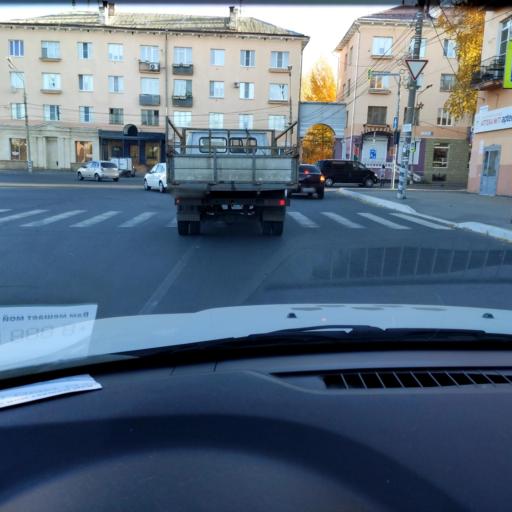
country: RU
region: Samara
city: Tol'yatti
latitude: 53.5134
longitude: 49.4105
